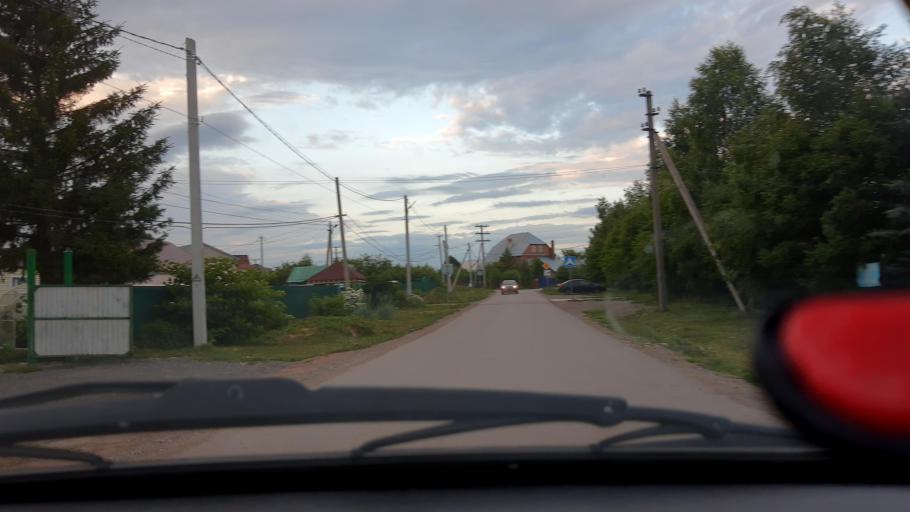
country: RU
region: Bashkortostan
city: Avdon
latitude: 54.4950
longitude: 55.8975
